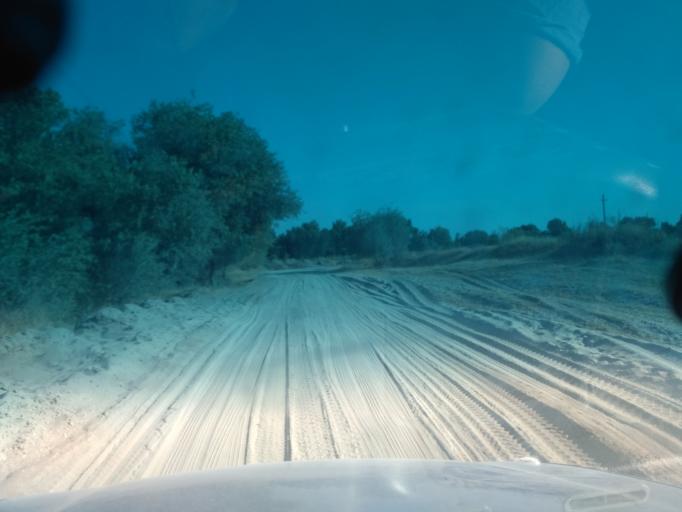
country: TJ
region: Viloyati Sughd
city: Buston
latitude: 40.5564
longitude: 69.0753
